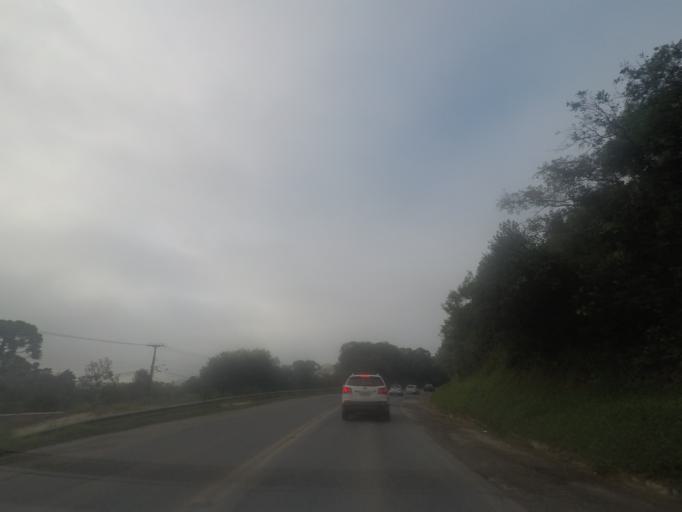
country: BR
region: Parana
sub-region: Almirante Tamandare
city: Almirante Tamandare
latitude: -25.3077
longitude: -49.3038
